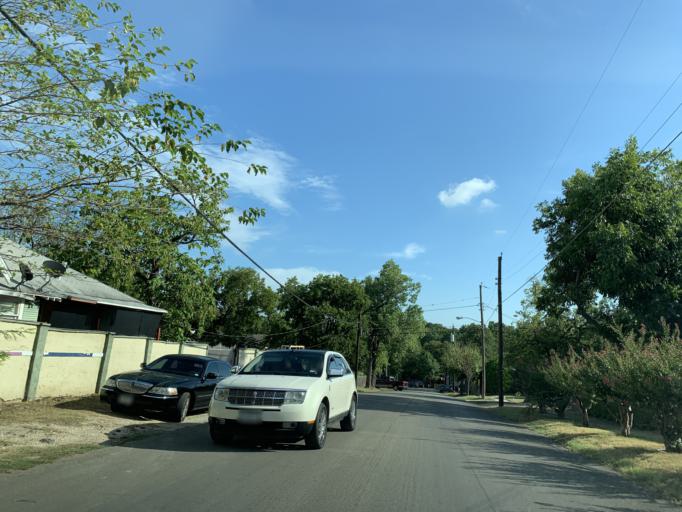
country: US
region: Texas
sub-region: Dallas County
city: Dallas
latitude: 32.7362
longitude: -96.8322
